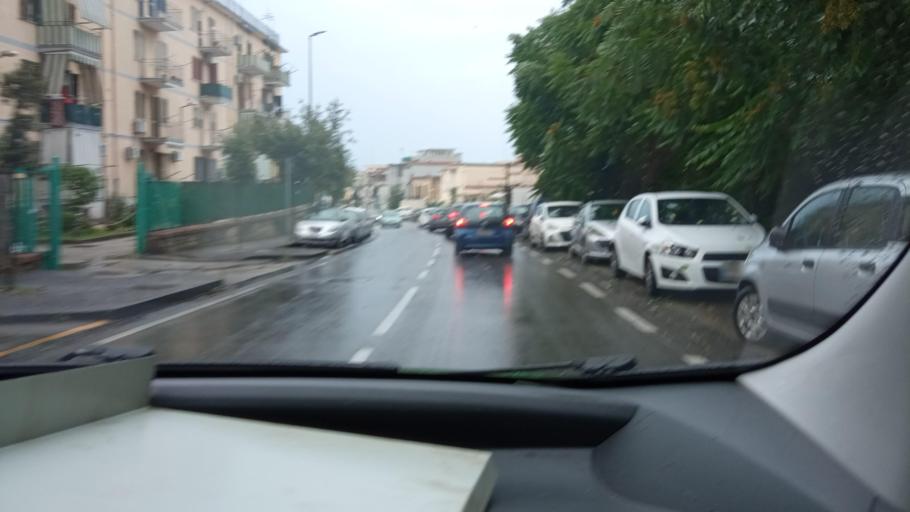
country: IT
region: Campania
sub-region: Provincia di Napoli
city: Pozzuoli
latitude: 40.8346
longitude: 14.1156
